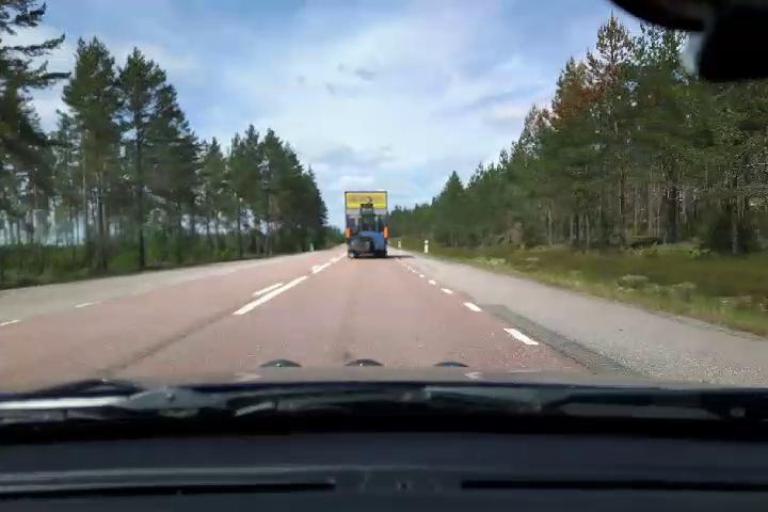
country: SE
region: Uppsala
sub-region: Osthammars Kommun
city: Bjorklinge
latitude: 60.1756
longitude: 17.4843
